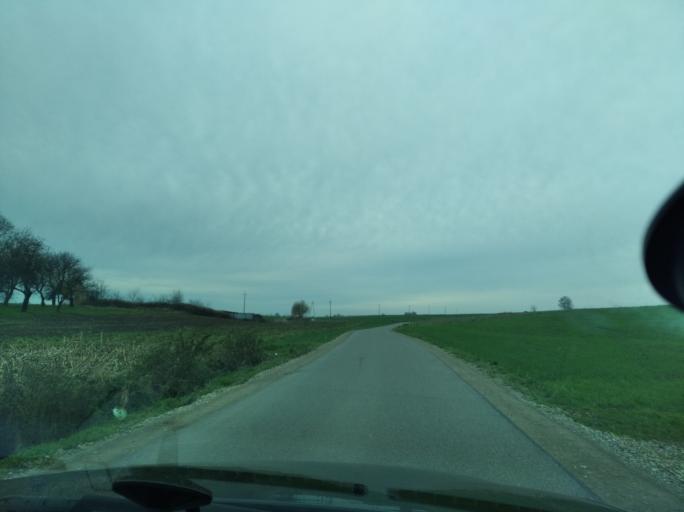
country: PL
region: Subcarpathian Voivodeship
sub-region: Powiat przeworski
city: Grzeska
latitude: 50.0654
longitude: 22.4681
